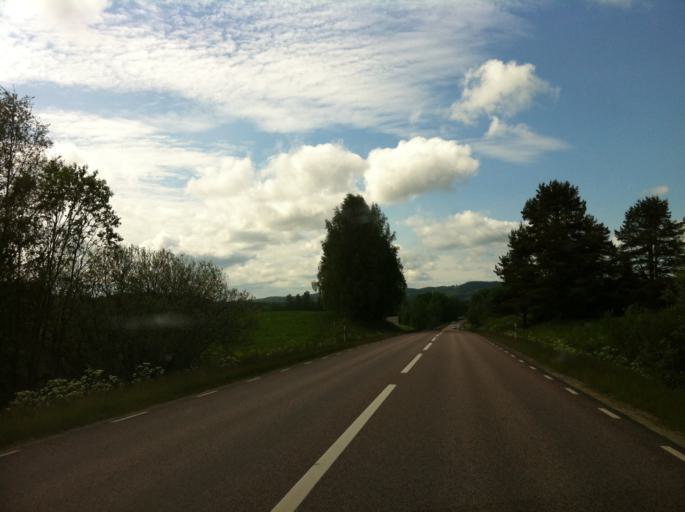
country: SE
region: Vaermland
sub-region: Sunne Kommun
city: Sunne
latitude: 59.7005
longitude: 13.1481
